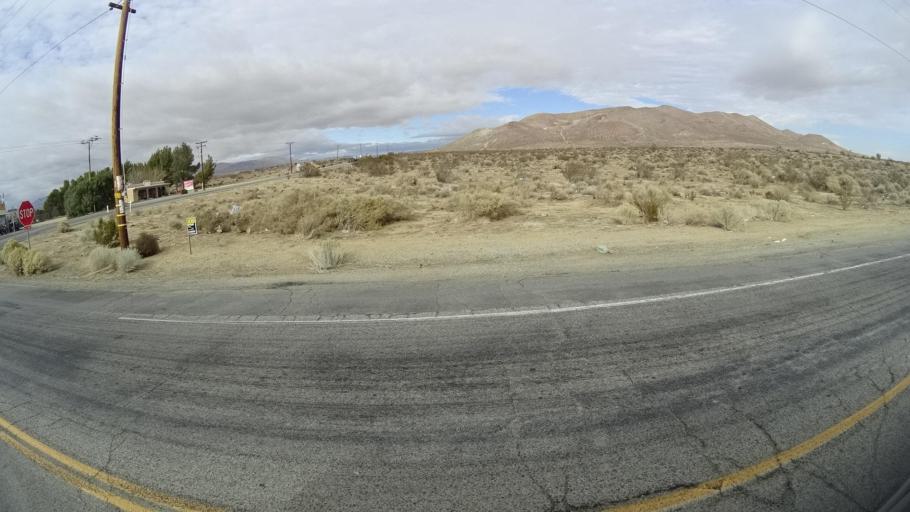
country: US
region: California
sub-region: Kern County
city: Rosamond
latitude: 34.8636
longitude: -118.2907
